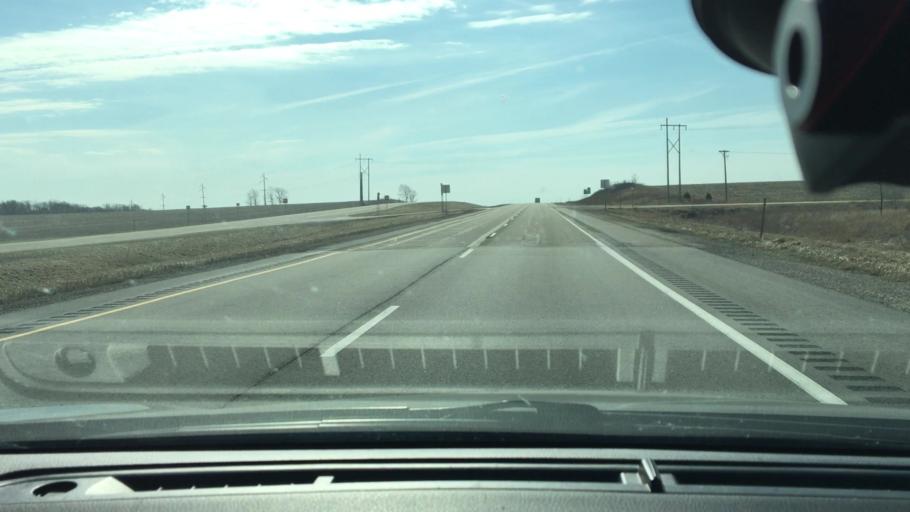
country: US
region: Iowa
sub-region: Floyd County
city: Charles City
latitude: 43.0028
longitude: -92.6141
